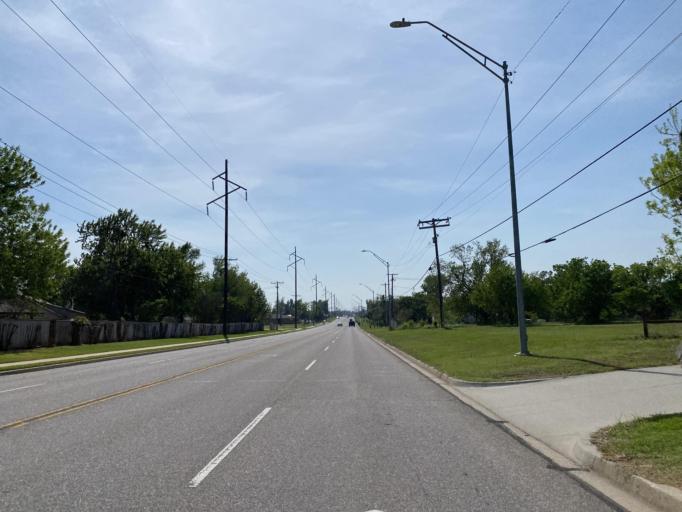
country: US
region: Oklahoma
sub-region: Oklahoma County
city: Nicoma Park
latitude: 35.4498
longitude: -97.3432
